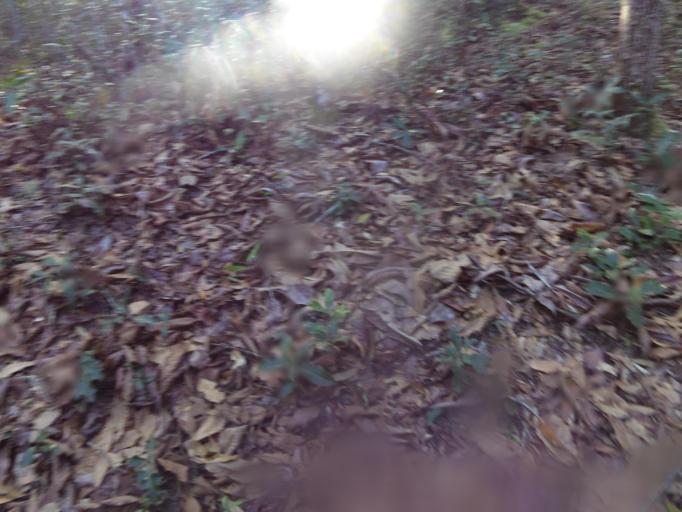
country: US
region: Florida
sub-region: Clay County
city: Middleburg
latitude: 30.1504
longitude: -81.9539
